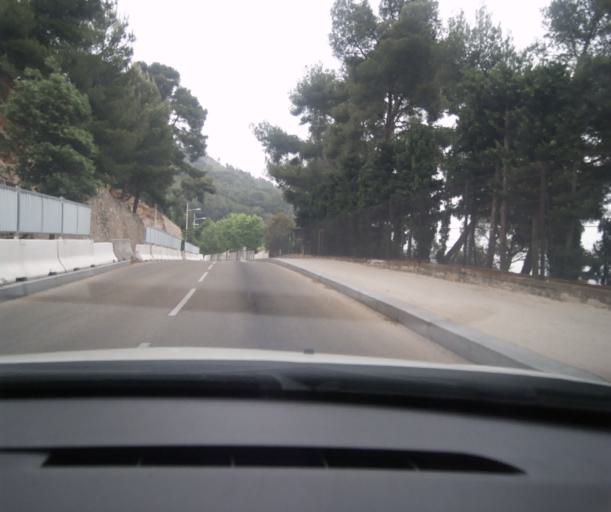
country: FR
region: Provence-Alpes-Cote d'Azur
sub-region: Departement du Var
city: La Valette-du-Var
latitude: 43.1332
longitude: 5.9574
